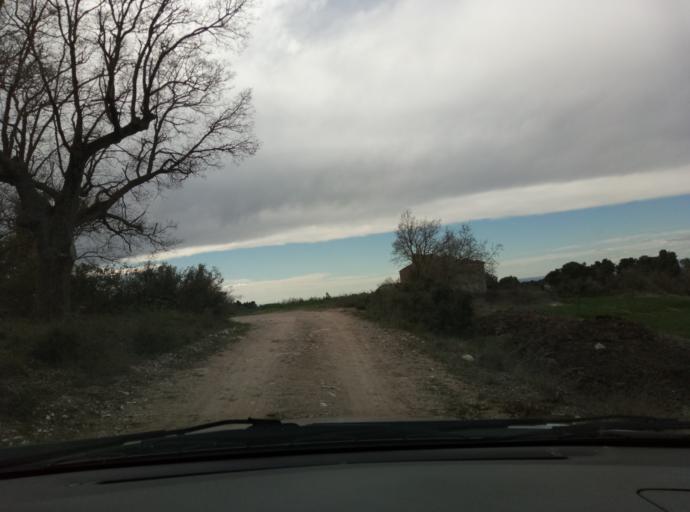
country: ES
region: Catalonia
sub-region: Provincia de Lleida
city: Ciutadilla
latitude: 41.5189
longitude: 1.1626
